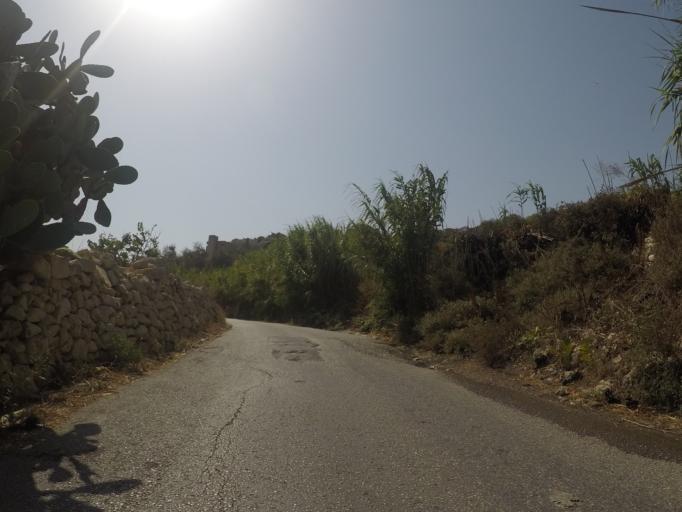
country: MT
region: L-Imgarr
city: Imgarr
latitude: 35.9381
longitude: 14.3786
